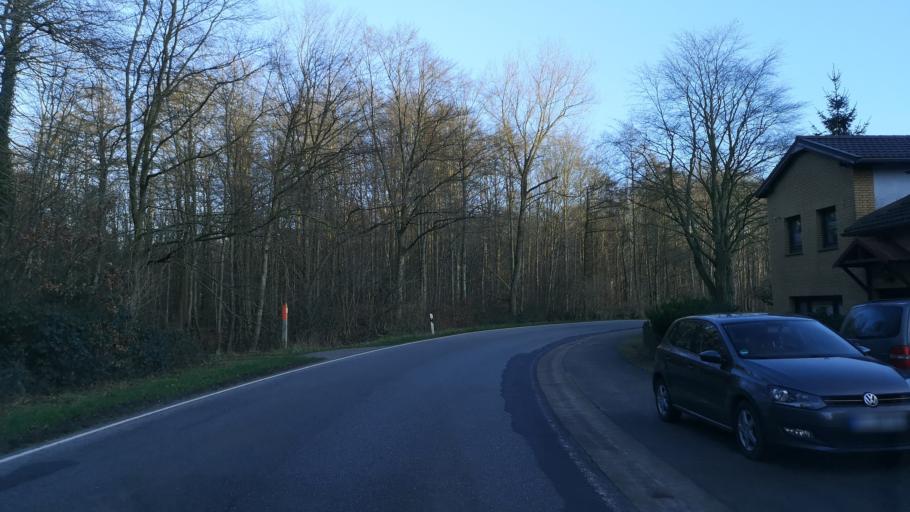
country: DE
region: Schleswig-Holstein
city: Ausacker
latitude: 54.6975
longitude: 9.5557
